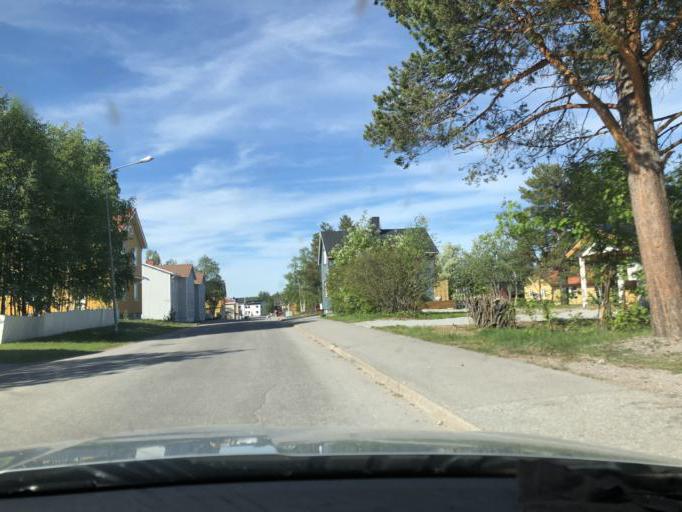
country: SE
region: Norrbotten
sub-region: Jokkmokks Kommun
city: Jokkmokk
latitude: 66.6042
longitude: 19.8299
